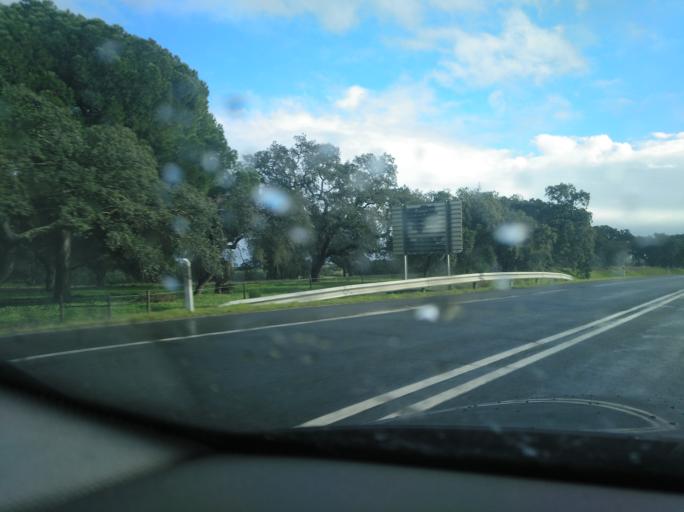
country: PT
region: Setubal
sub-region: Grandola
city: Grandola
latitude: 38.0536
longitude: -8.4029
